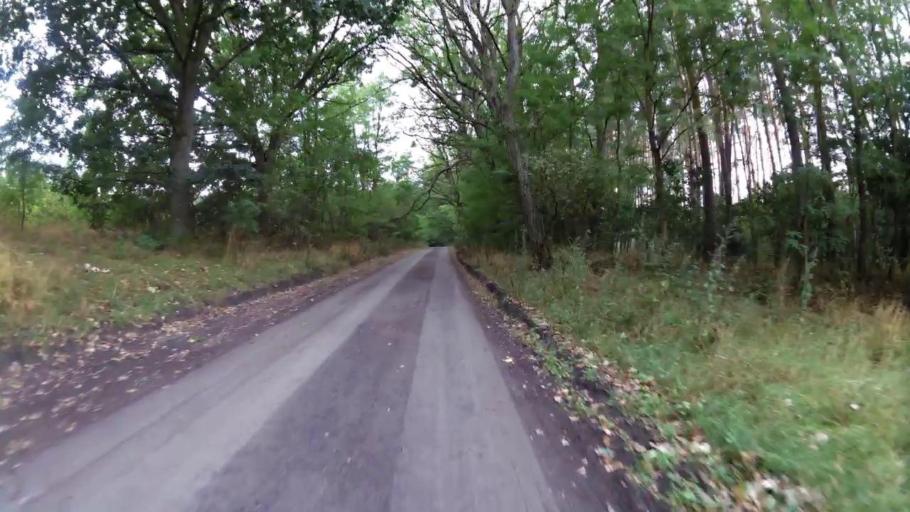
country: PL
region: West Pomeranian Voivodeship
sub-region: Powiat mysliborski
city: Debno
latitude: 52.8138
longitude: 14.7259
